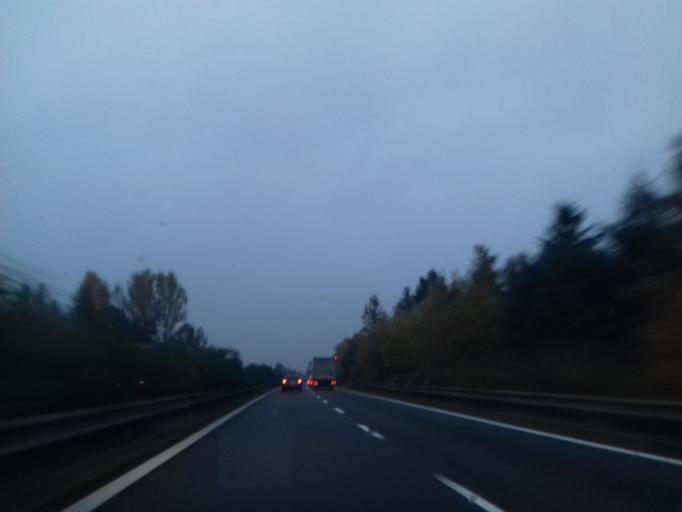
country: CZ
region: Olomoucky
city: Litovel
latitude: 49.6856
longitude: 17.0559
